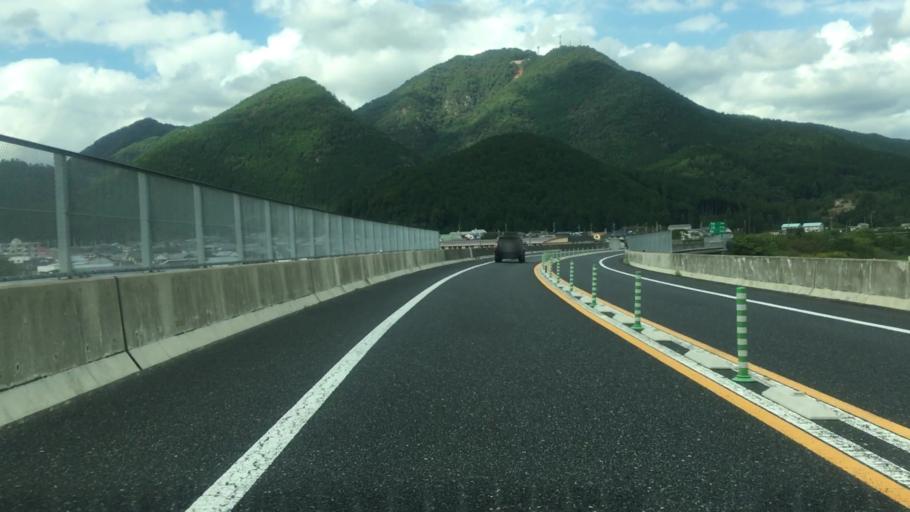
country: JP
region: Kyoto
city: Fukuchiyama
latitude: 35.1784
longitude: 135.0375
